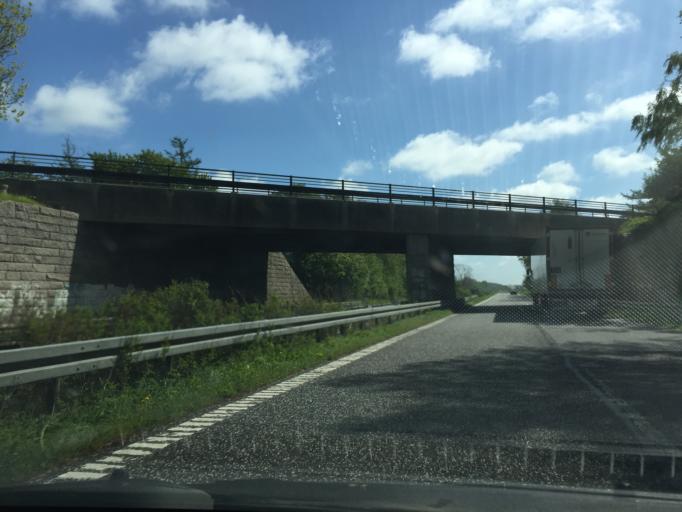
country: DK
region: Zealand
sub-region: Lolland Kommune
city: Maribo
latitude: 54.7624
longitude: 11.4621
